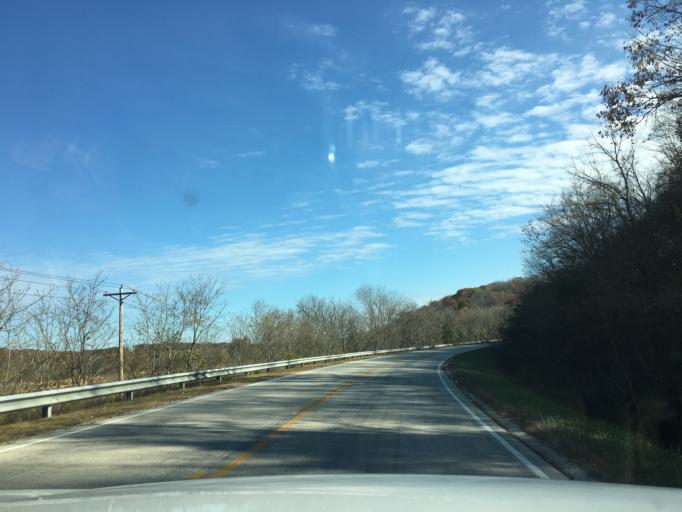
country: US
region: Missouri
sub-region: Osage County
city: Linn
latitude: 38.3882
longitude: -91.8171
